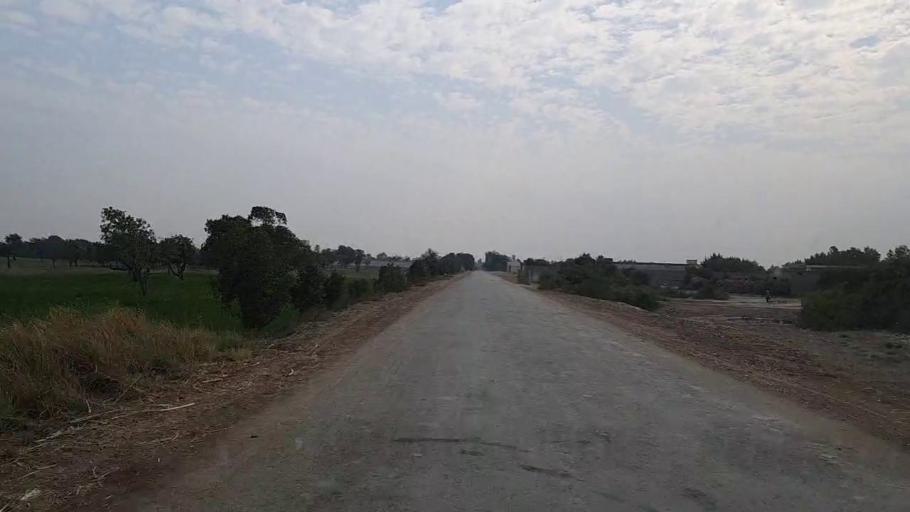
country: PK
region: Sindh
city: Mirwah Gorchani
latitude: 25.3743
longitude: 69.0817
